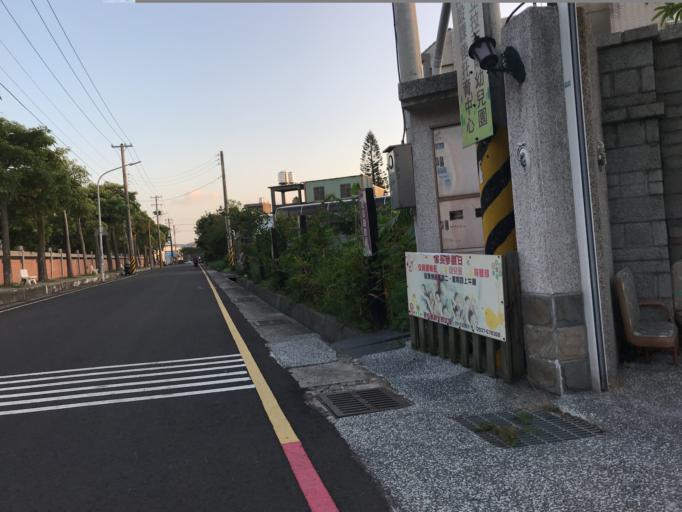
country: TW
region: Taiwan
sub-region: Hsinchu
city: Hsinchu
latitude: 24.8066
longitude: 120.9403
